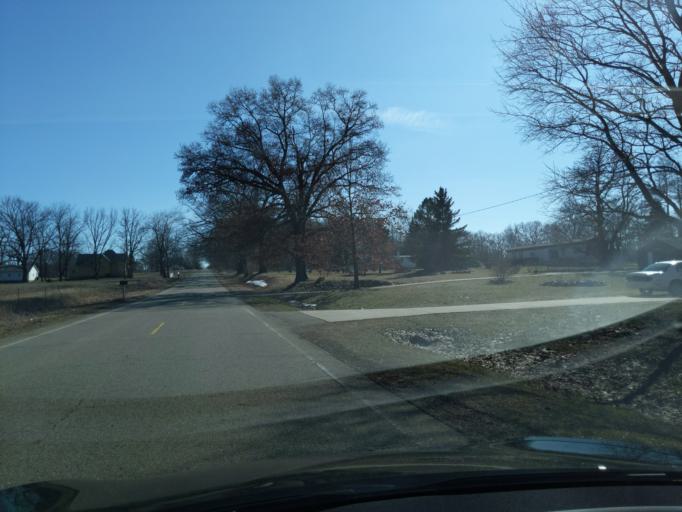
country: US
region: Michigan
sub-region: Ingham County
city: Leslie
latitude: 42.4032
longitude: -84.4434
